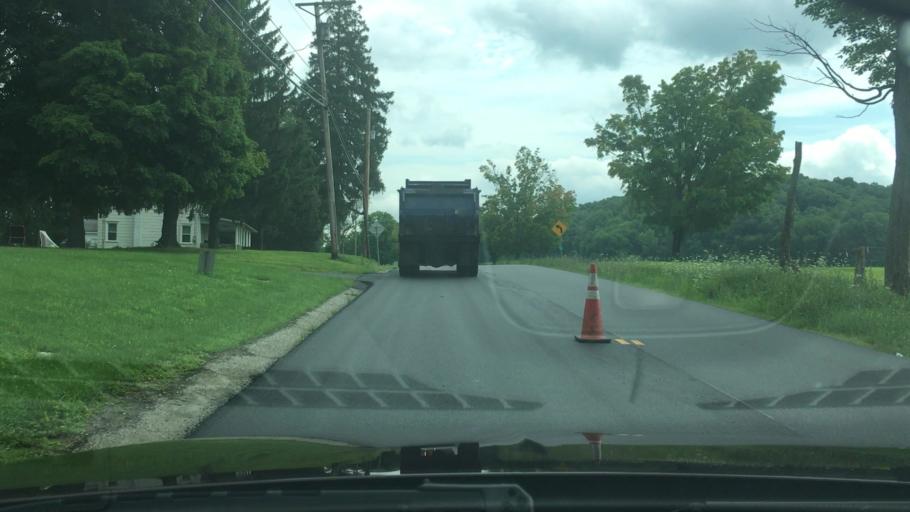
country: US
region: New York
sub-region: Dutchess County
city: Hillside Lake
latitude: 41.5808
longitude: -73.7304
